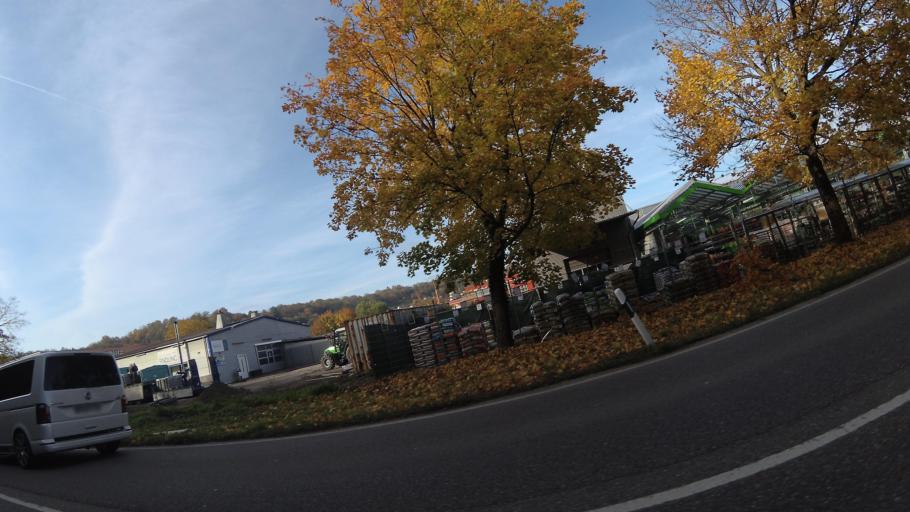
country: DE
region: Baden-Wuerttemberg
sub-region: Regierungsbezirk Stuttgart
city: Mockmuhl
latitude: 49.3174
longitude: 9.3641
